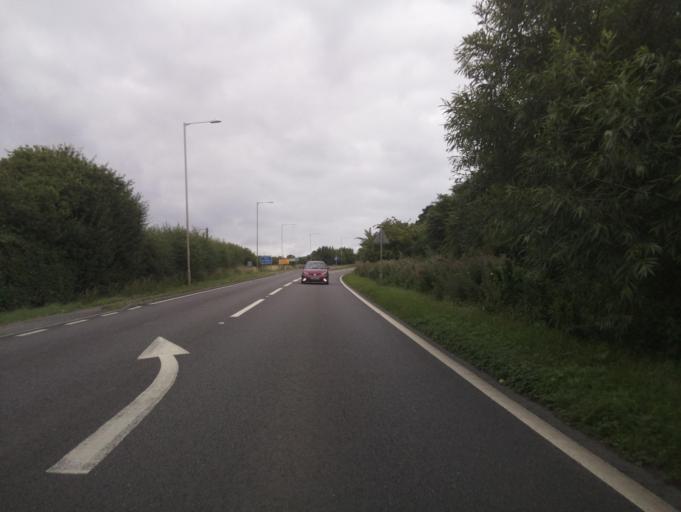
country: GB
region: England
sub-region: Lincolnshire
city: Barrowby
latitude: 52.9235
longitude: -0.6929
